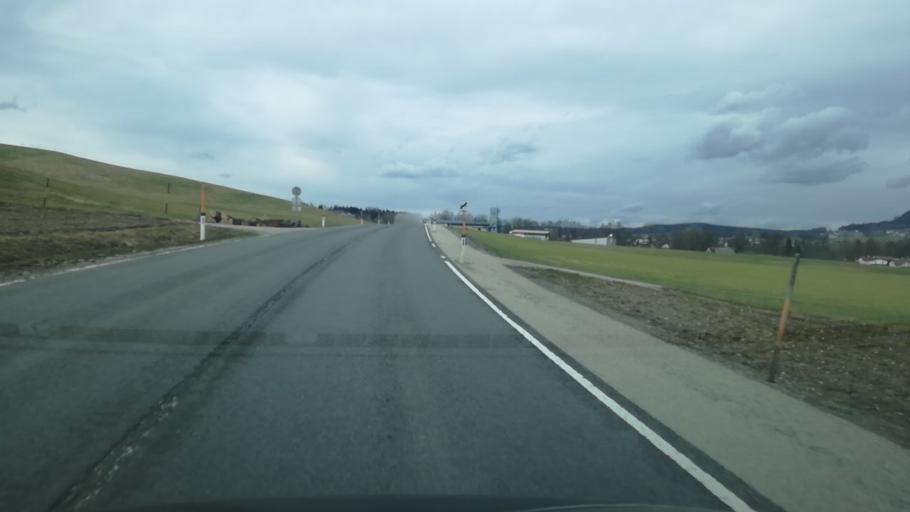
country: AT
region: Upper Austria
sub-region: Politischer Bezirk Vocklabruck
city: Frankenburg
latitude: 48.0478
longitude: 13.4861
